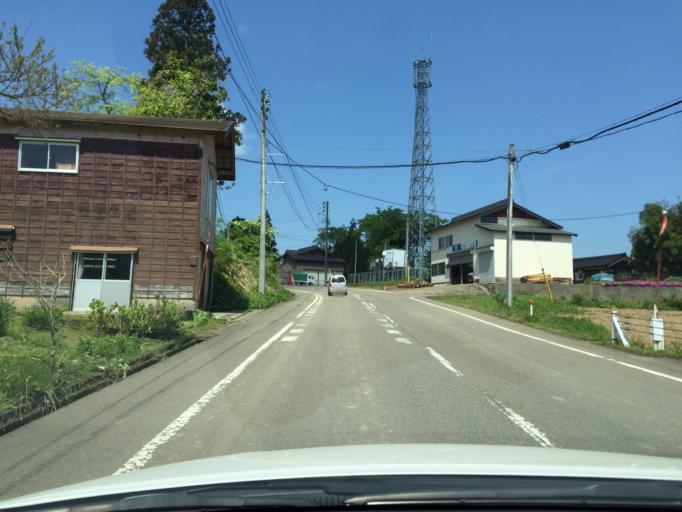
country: JP
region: Niigata
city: Tochio-honcho
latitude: 37.4763
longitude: 139.0459
